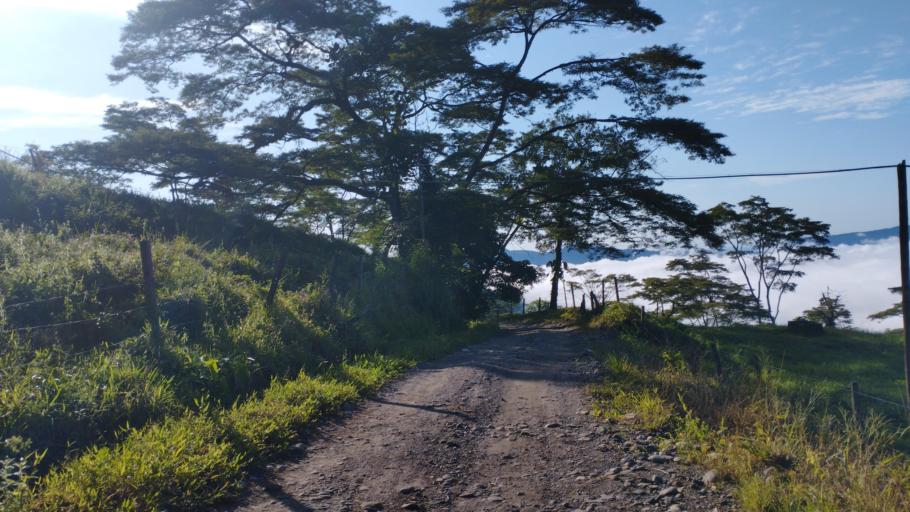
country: CO
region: Boyaca
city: San Luis de Gaceno
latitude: 4.7899
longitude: -73.0978
